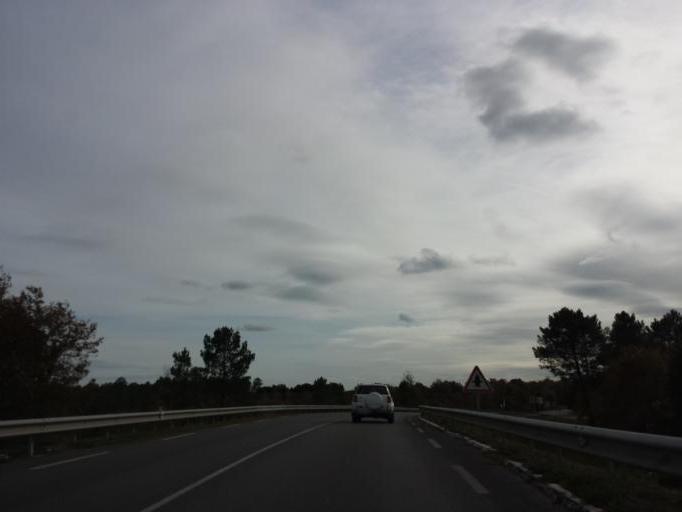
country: FR
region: Aquitaine
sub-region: Departement de la Gironde
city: Marcheprime
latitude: 44.7828
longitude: -0.9322
